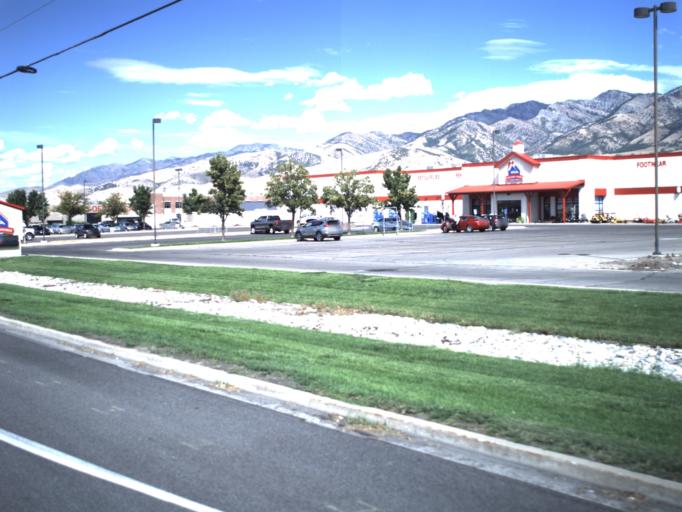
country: US
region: Utah
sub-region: Cache County
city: North Logan
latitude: 41.7727
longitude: -111.8340
